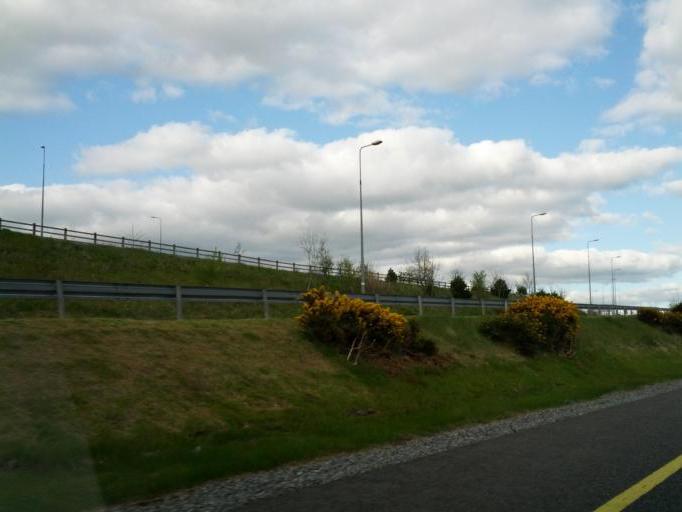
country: IE
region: Leinster
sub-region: An Iarmhi
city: Moate
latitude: 53.3863
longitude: -7.6876
